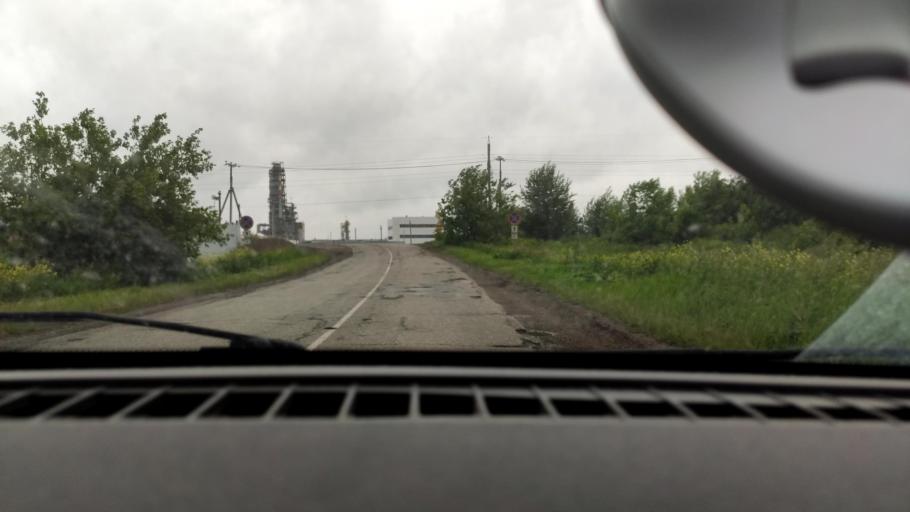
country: RU
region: Perm
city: Gamovo
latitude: 57.9042
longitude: 56.1219
